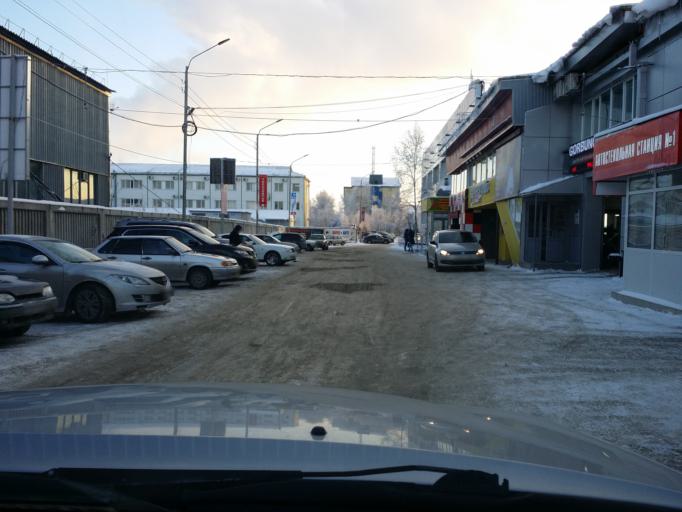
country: RU
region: Khanty-Mansiyskiy Avtonomnyy Okrug
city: Nizhnevartovsk
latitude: 60.9408
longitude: 76.5382
